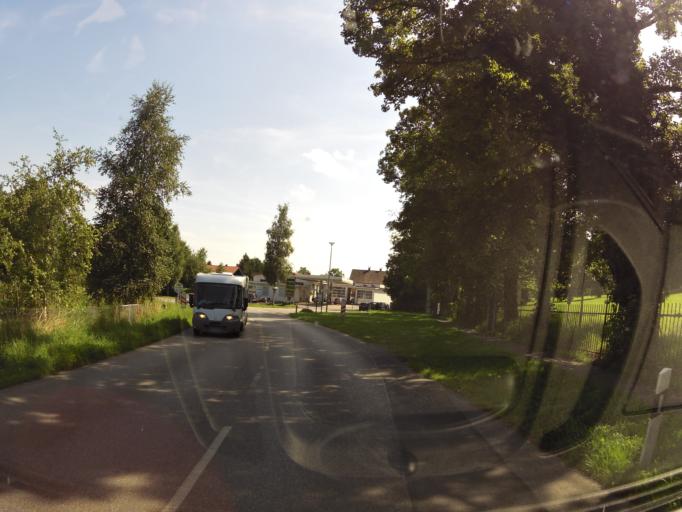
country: DE
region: Bavaria
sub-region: Upper Bavaria
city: Diessen am Ammersee
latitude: 47.9417
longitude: 11.1047
